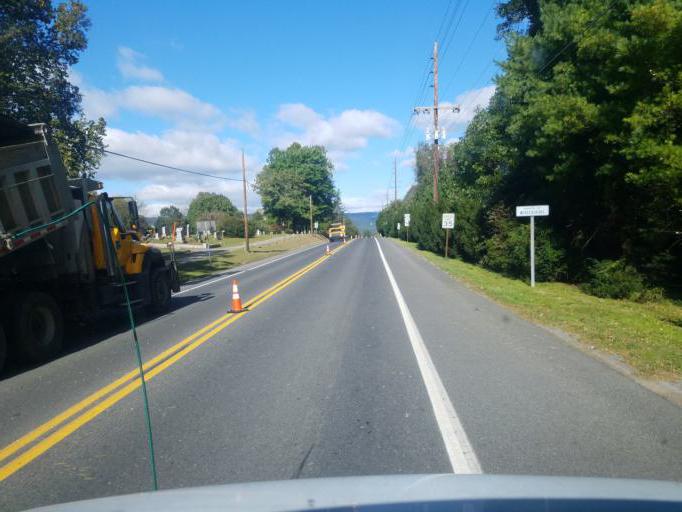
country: US
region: Pennsylvania
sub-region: Franklin County
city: Mercersburg
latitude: 39.8221
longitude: -77.8995
